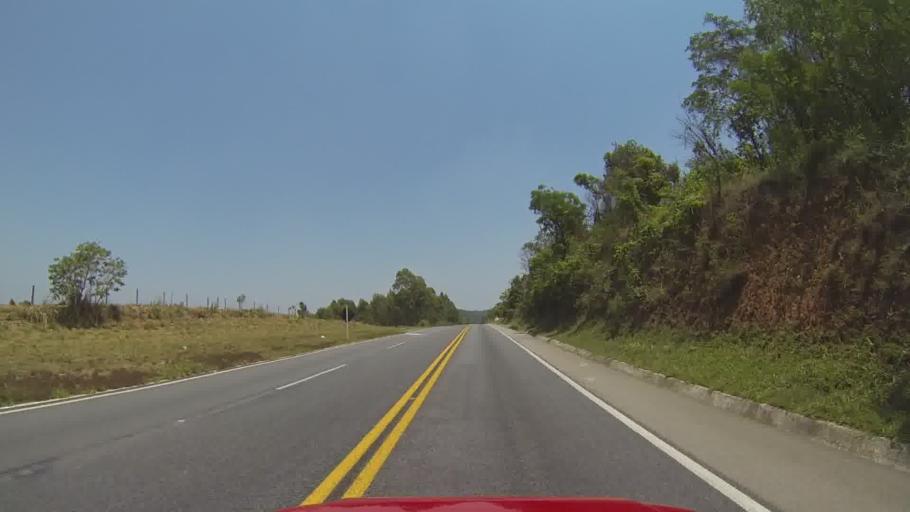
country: BR
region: Minas Gerais
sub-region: Itapecerica
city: Itapecerica
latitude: -20.2808
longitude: -45.1369
